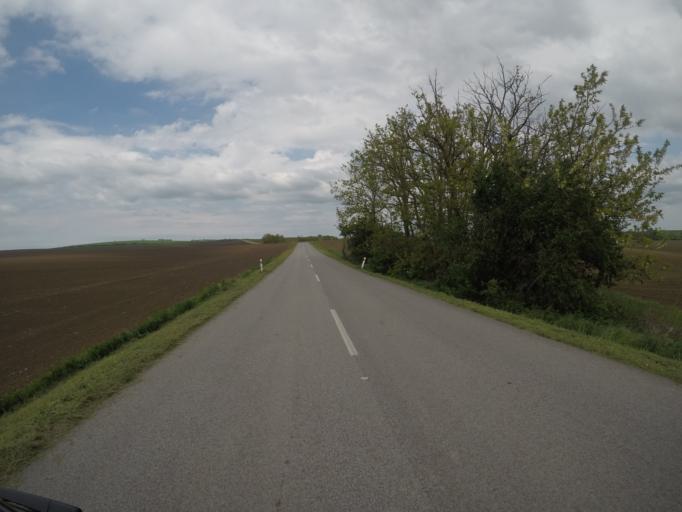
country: SK
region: Nitriansky
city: Zeliezovce
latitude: 48.0341
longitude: 18.8028
